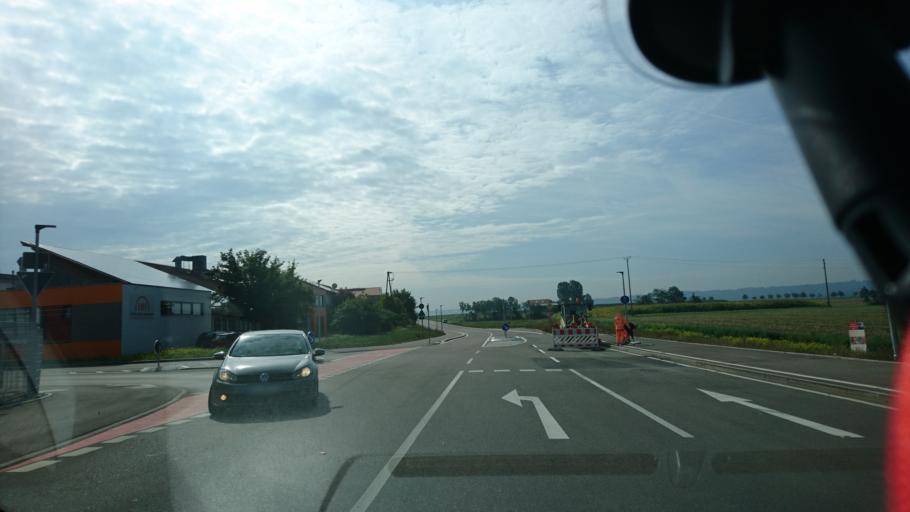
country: DE
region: Baden-Wuerttemberg
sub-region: Regierungsbezirk Stuttgart
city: Michelfeld
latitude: 49.1018
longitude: 9.6918
